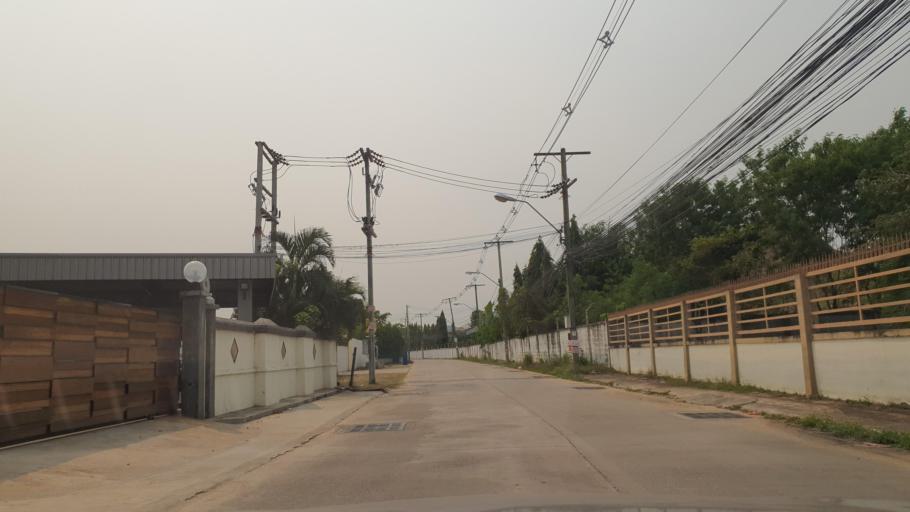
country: TH
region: Chon Buri
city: Phatthaya
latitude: 12.8919
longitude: 100.8916
